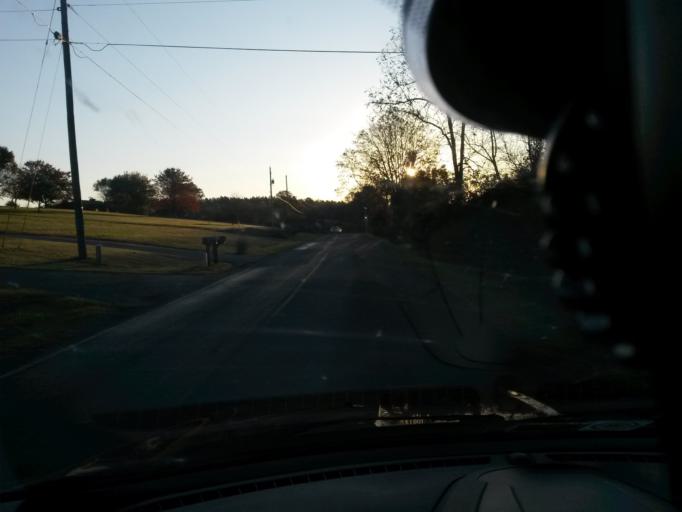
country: US
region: Virginia
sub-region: Roanoke County
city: Narrows
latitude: 37.1663
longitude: -79.8681
